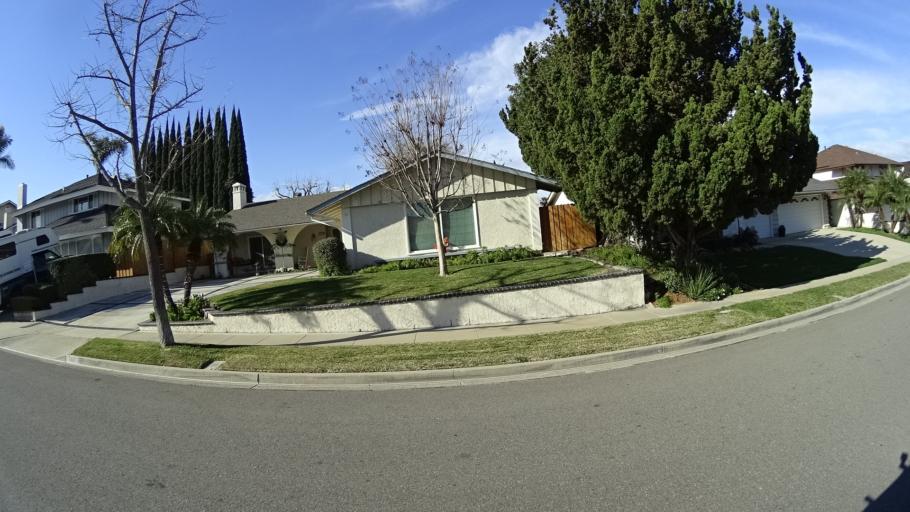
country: US
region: California
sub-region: Orange County
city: Villa Park
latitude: 33.8468
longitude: -117.8242
